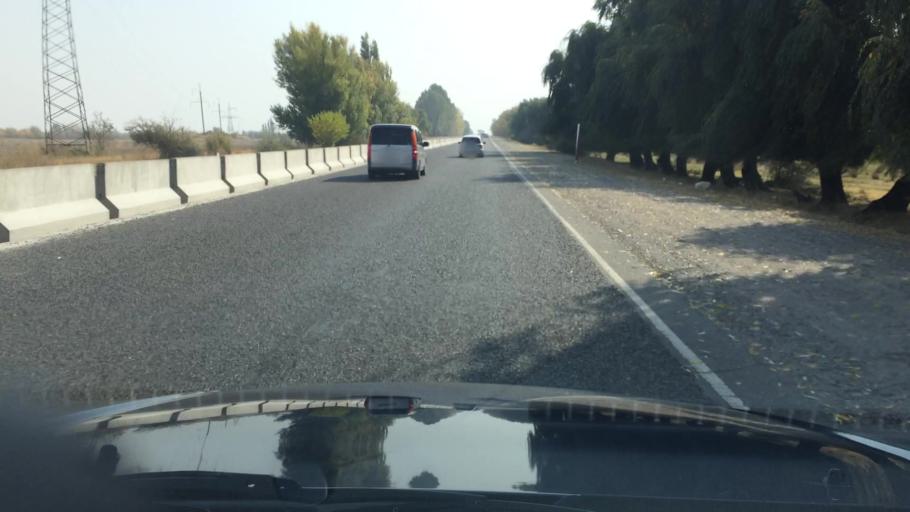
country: KG
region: Chuy
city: Kant
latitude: 42.9665
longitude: 74.9102
